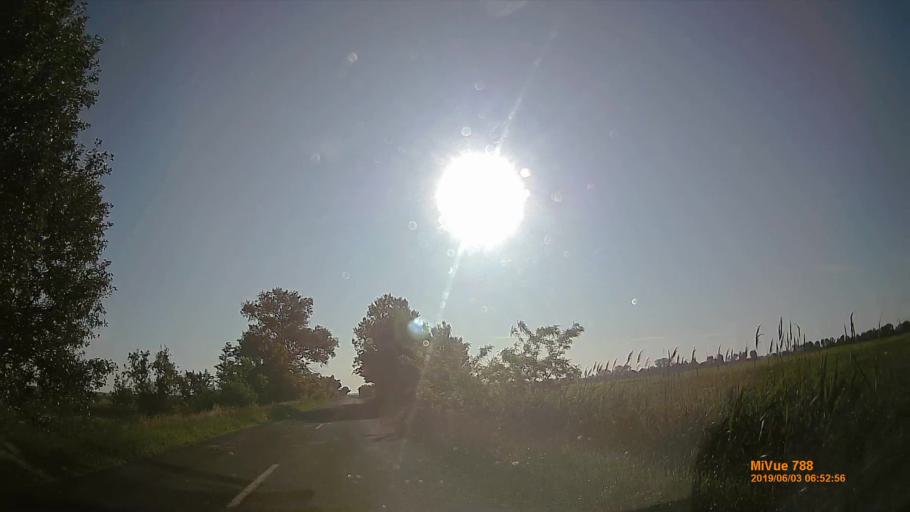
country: HU
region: Pest
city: Bugyi
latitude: 47.2043
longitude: 19.2036
